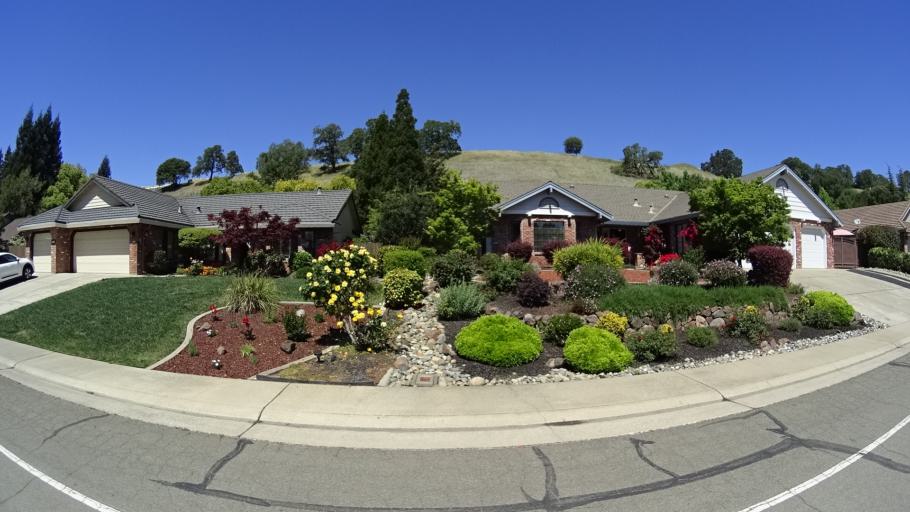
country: US
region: California
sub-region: Placer County
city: Rocklin
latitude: 38.8077
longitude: -121.2315
